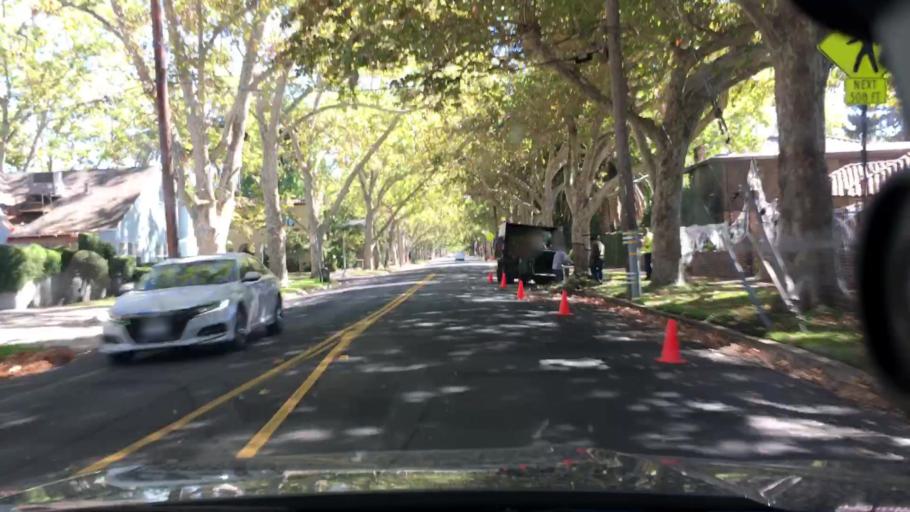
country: US
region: California
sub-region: Sacramento County
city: Sacramento
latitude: 38.5740
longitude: -121.4604
